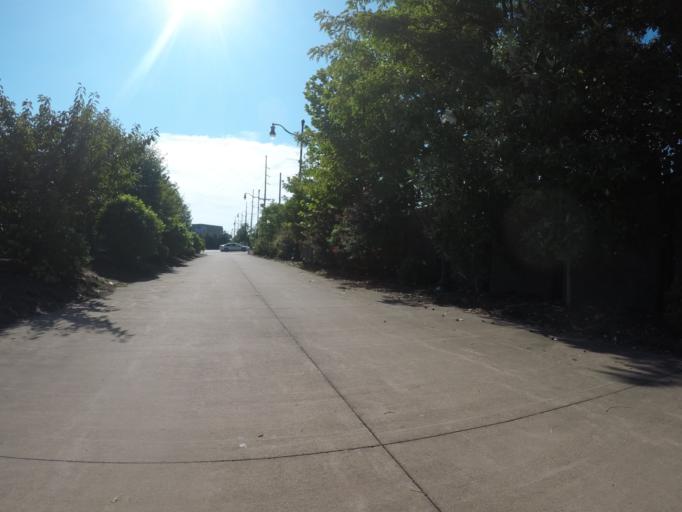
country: US
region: Kentucky
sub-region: Boyd County
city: Ashland
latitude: 38.4816
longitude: -82.6397
